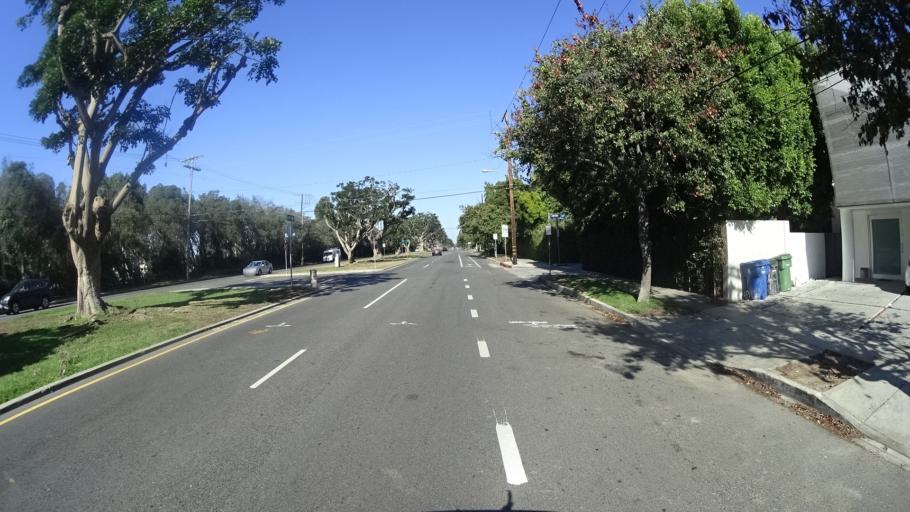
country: US
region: California
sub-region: Los Angeles County
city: Santa Monica
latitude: 34.0505
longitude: -118.4818
